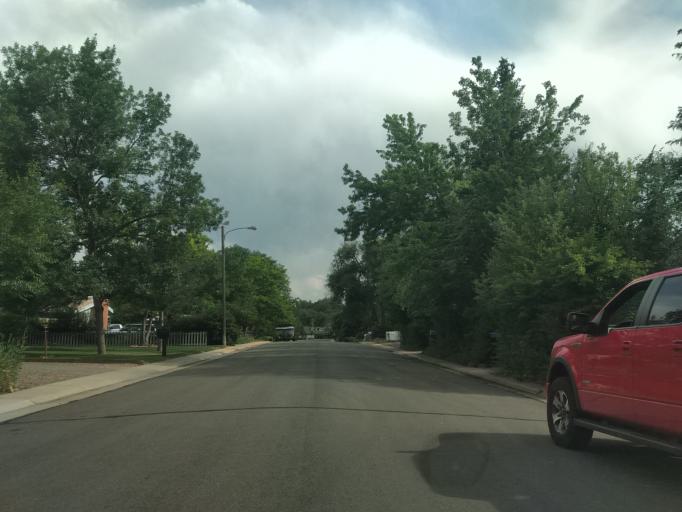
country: US
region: Colorado
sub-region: Jefferson County
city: Lakewood
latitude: 39.7030
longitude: -105.0922
